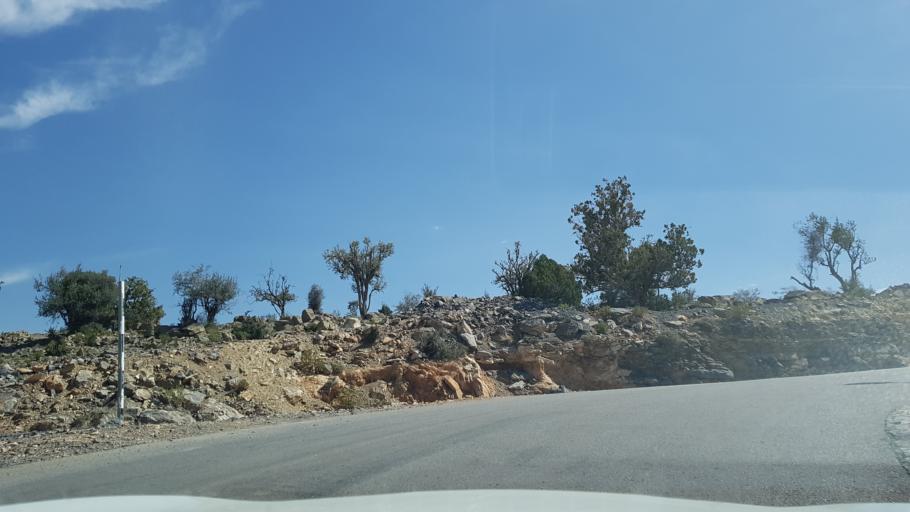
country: OM
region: Al Batinah
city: Bayt al `Awabi
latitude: 23.1329
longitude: 57.5978
